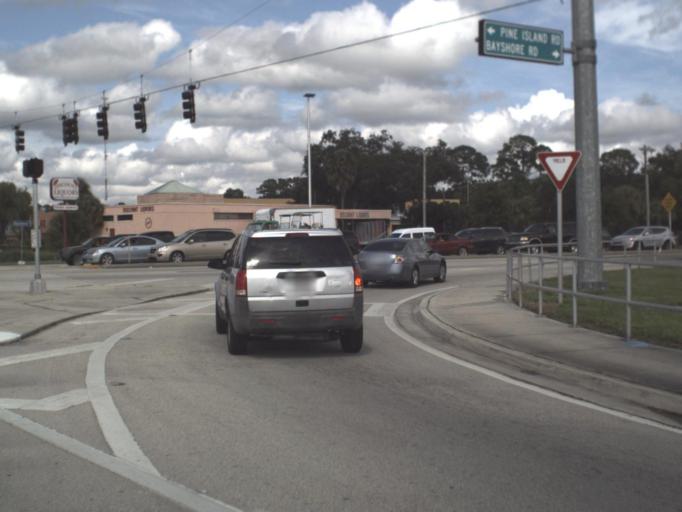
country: US
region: Florida
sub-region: Lee County
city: Palmona Park
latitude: 26.6817
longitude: -81.8833
